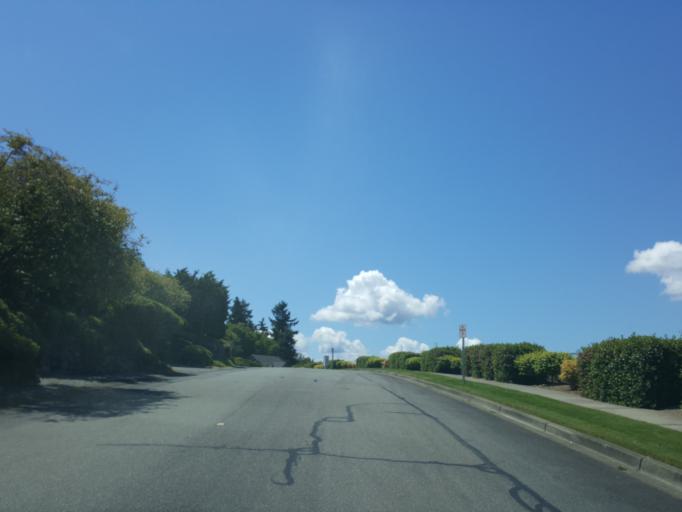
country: US
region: Washington
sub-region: Pierce County
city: University Place
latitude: 47.2150
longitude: -122.5724
